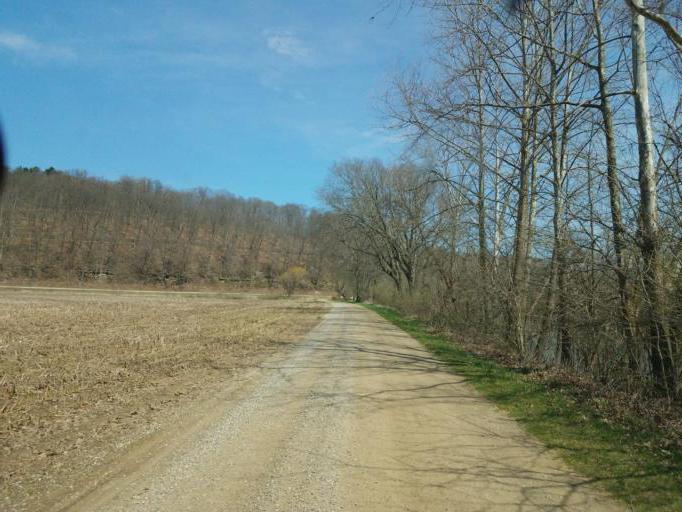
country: US
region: Ohio
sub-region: Knox County
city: Oak Hill
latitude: 40.3814
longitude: -82.2318
